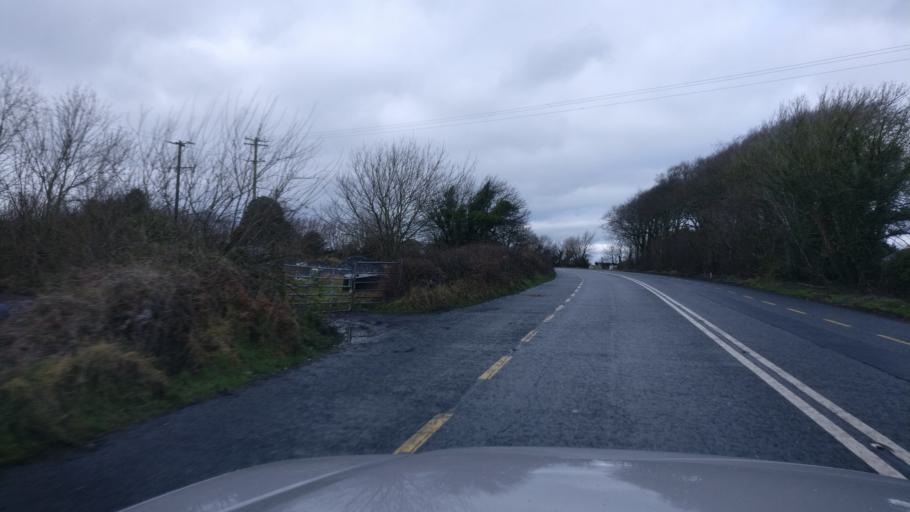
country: IE
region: Connaught
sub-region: County Galway
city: Athenry
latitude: 53.2683
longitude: -8.8287
